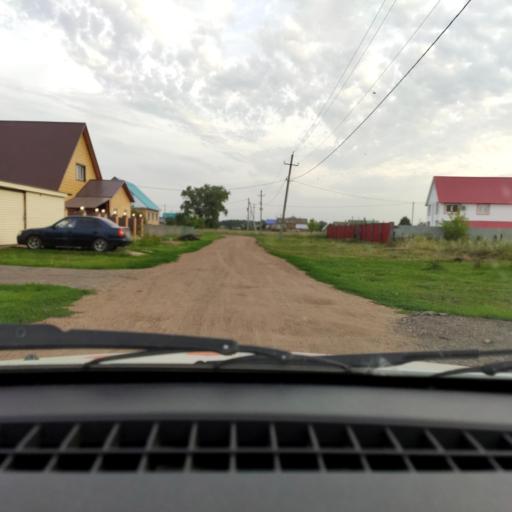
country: RU
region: Bashkortostan
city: Blagoveshchensk
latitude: 54.9293
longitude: 55.9720
